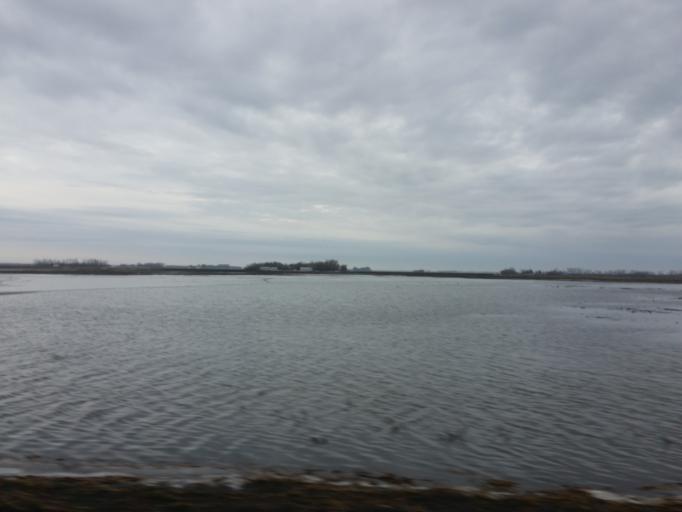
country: US
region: North Dakota
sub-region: Walsh County
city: Grafton
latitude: 48.3932
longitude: -97.4486
